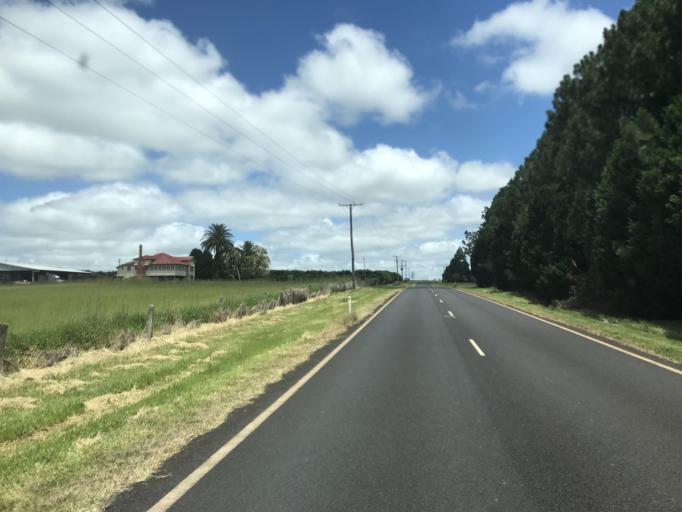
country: AU
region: Queensland
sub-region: Tablelands
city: Ravenshoe
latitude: -17.5082
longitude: 145.4662
